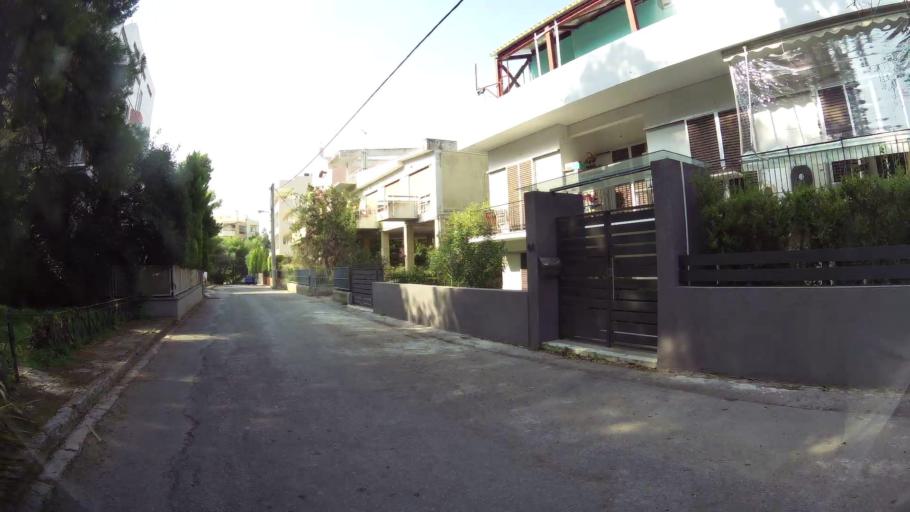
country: GR
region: Attica
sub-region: Nomarchia Athinas
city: Papagou
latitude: 37.9833
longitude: 23.7886
